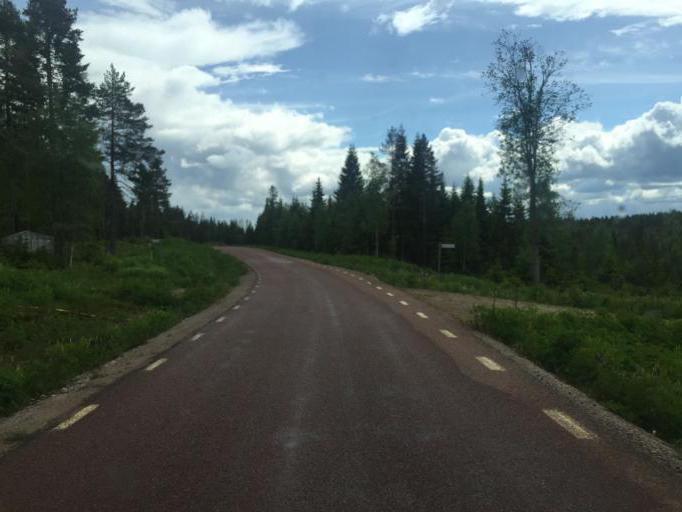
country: SE
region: Vaermland
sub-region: Hagfors Kommun
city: Hagfors
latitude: 60.3085
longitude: 13.8655
